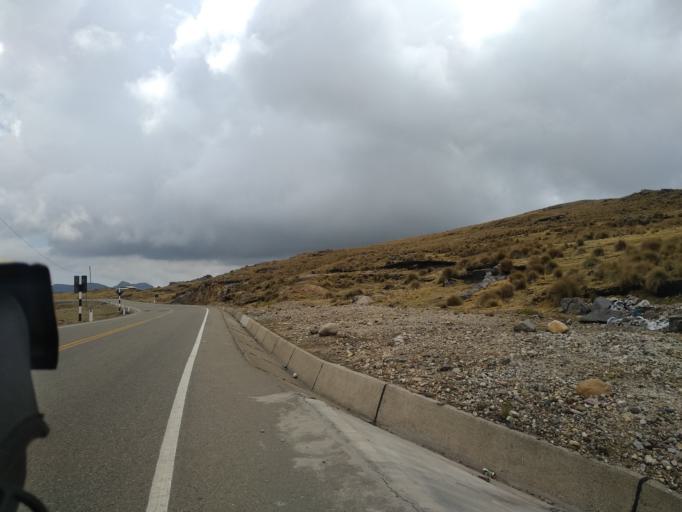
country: PE
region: La Libertad
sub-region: Provincia de Santiago de Chuco
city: Quiruvilca
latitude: -7.9691
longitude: -78.2006
